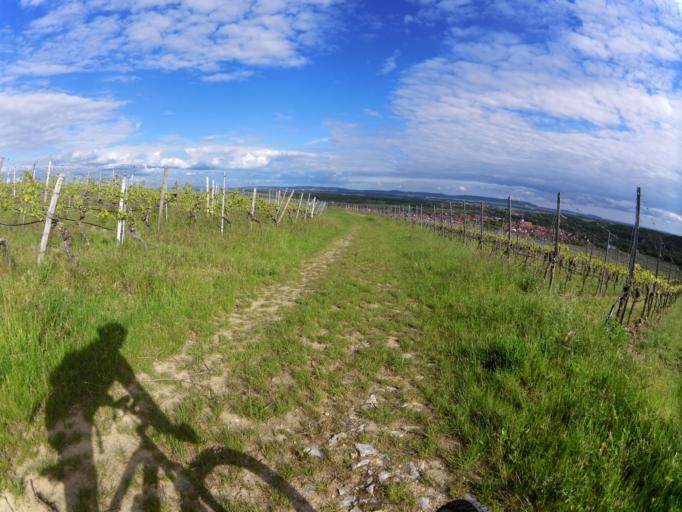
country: DE
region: Bavaria
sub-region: Regierungsbezirk Unterfranken
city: Sommerach
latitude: 49.8375
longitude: 10.1993
